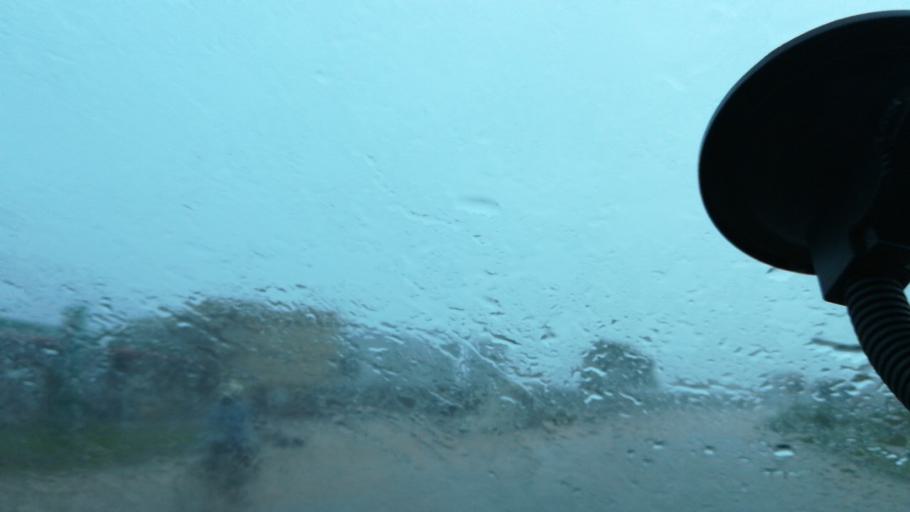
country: CD
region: Katanga
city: Lubumbashi
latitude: -11.5917
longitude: 27.4983
